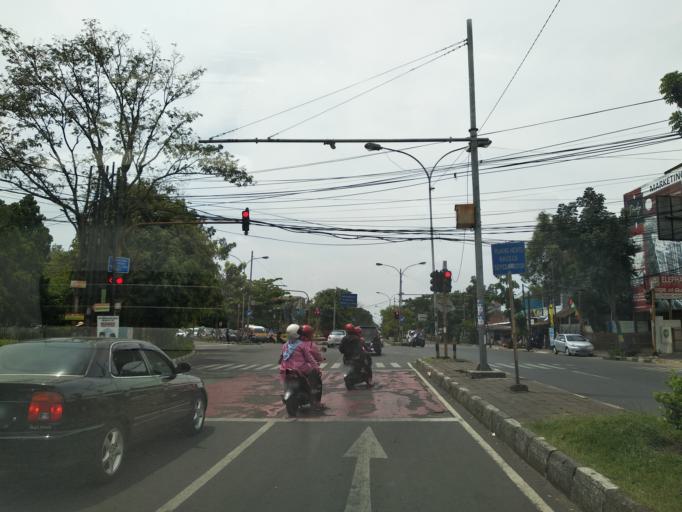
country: ID
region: West Java
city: Bandung
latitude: -6.9377
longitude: 107.6088
